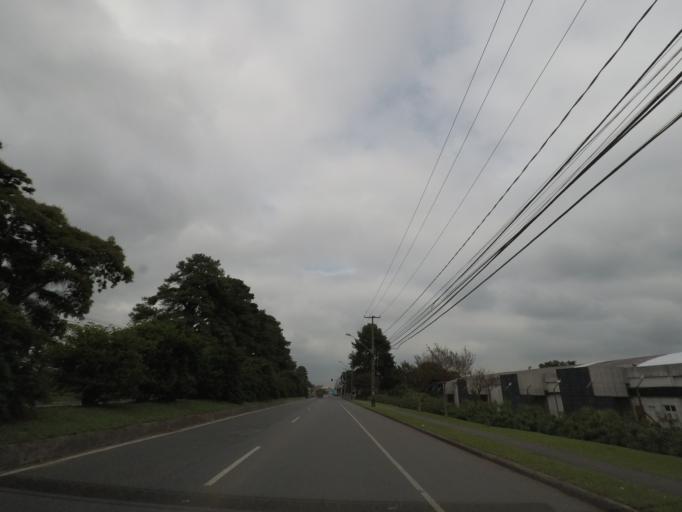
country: BR
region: Parana
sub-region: Curitiba
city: Curitiba
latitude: -25.5040
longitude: -49.3283
